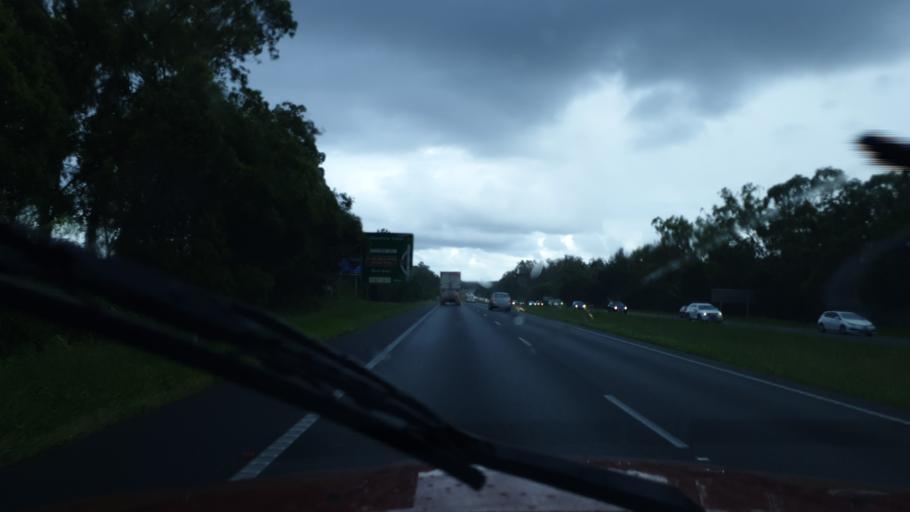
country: AU
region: Queensland
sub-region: Moreton Bay
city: Caboolture
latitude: -27.0027
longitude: 152.9773
